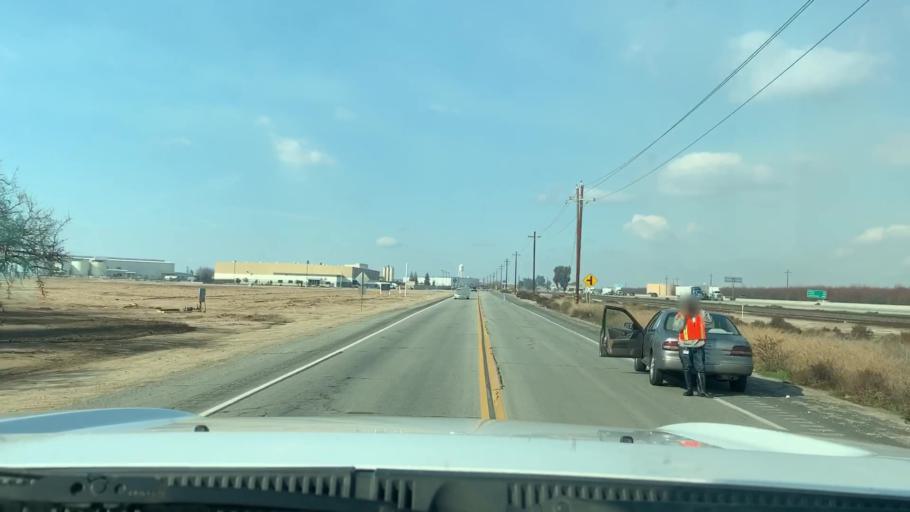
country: US
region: California
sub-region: Kern County
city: Rosedale
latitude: 35.4909
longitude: -119.1541
